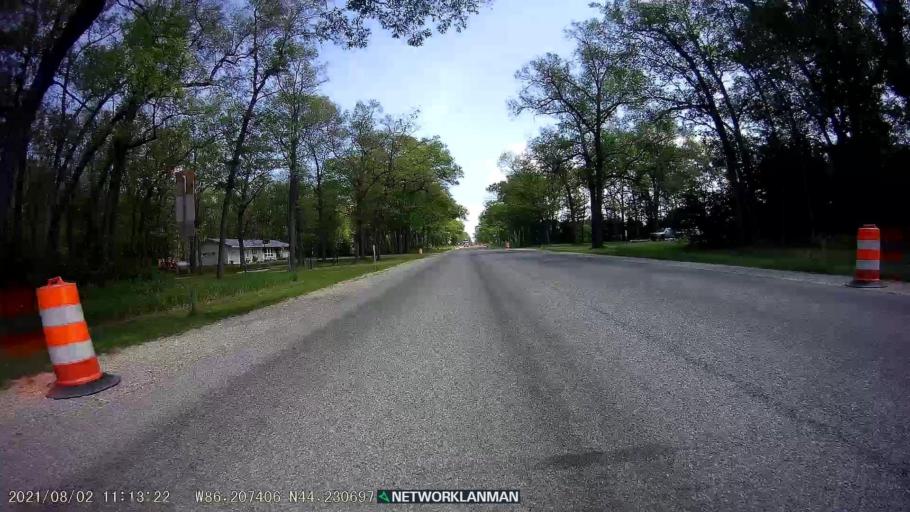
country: US
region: Michigan
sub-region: Manistee County
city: Manistee
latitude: 44.2307
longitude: -86.2075
